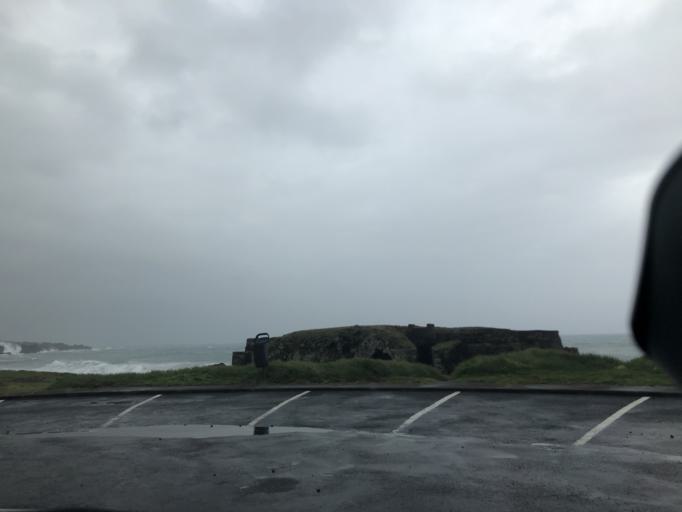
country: PT
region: Azores
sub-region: Ponta Delgada
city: Rosto de Cao
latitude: 37.7497
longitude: -25.6218
